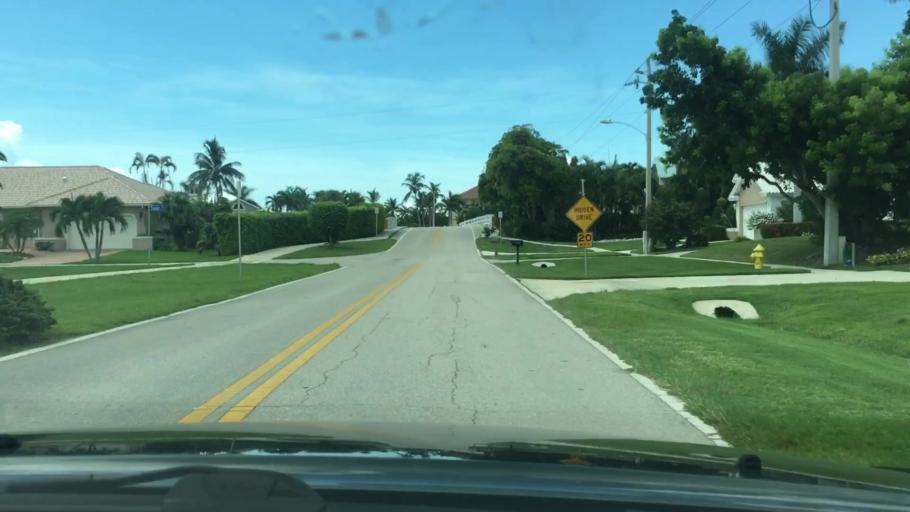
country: US
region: Florida
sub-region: Collier County
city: Marco
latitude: 25.9512
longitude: -81.7410
